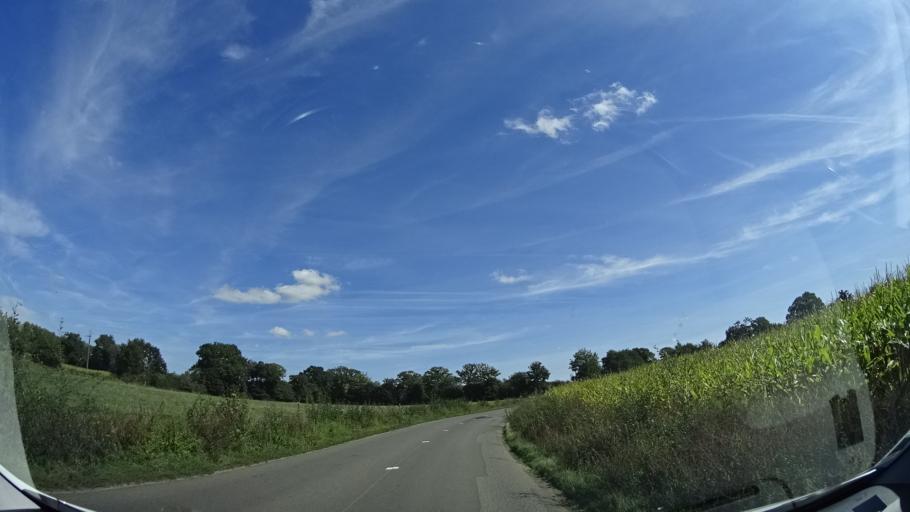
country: FR
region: Brittany
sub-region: Departement d'Ille-et-Vilaine
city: Saint-Sulpice-la-Foret
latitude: 48.2189
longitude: -1.5669
